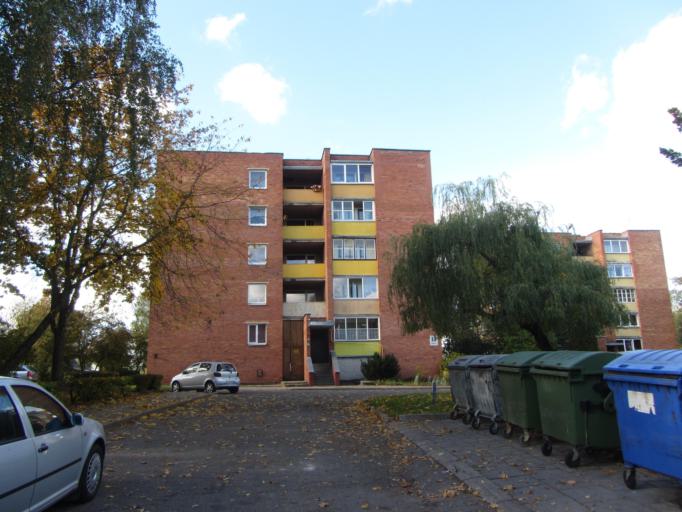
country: LT
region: Utenos apskritis
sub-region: Utena
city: Utena
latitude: 55.5090
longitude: 25.6094
